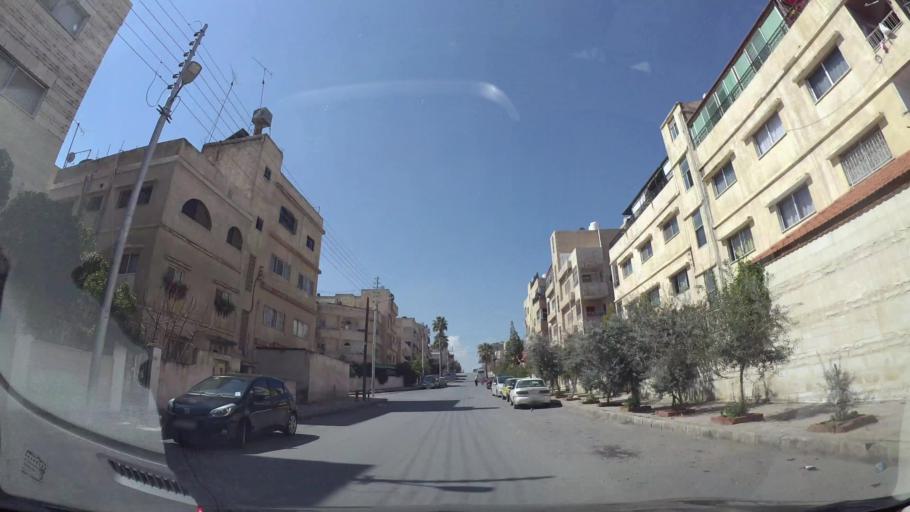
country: JO
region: Amman
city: Amman
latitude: 31.9789
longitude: 35.9943
